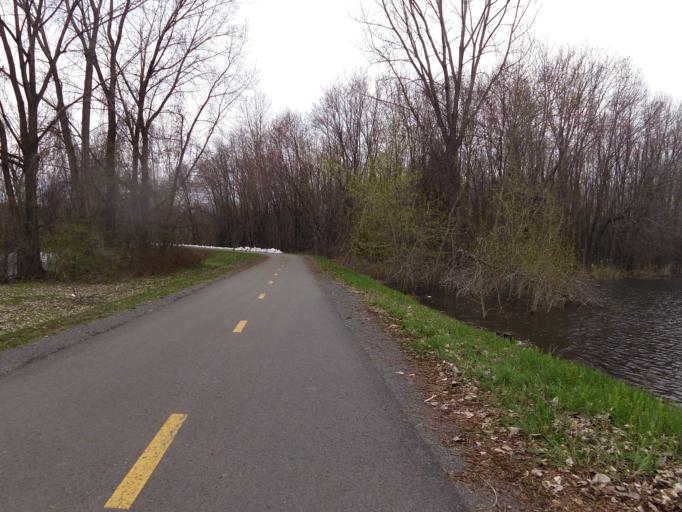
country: CA
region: Quebec
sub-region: Laurentides
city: Sainte-Marthe-sur-le-Lac
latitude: 45.5038
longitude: -73.9787
